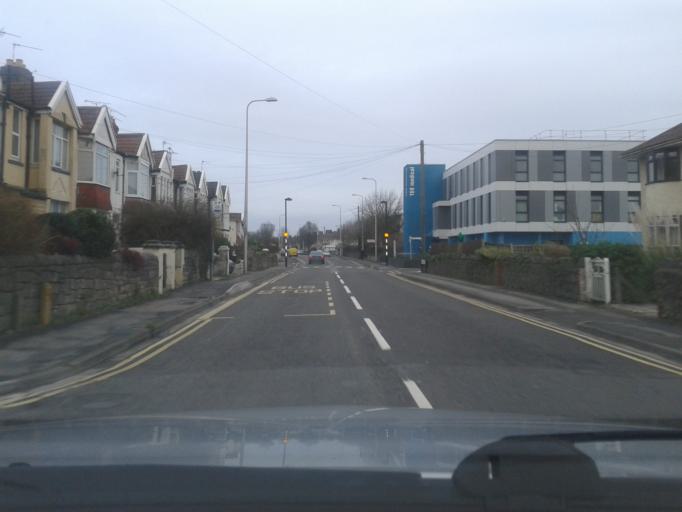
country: GB
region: England
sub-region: North Somerset
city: Weston-super-Mare
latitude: 51.3457
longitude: -2.9585
